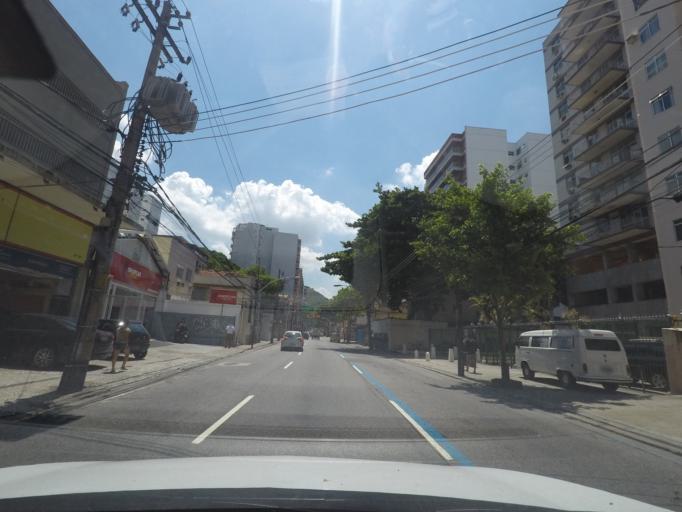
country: BR
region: Rio de Janeiro
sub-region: Rio De Janeiro
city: Rio de Janeiro
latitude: -22.9170
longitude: -43.2559
